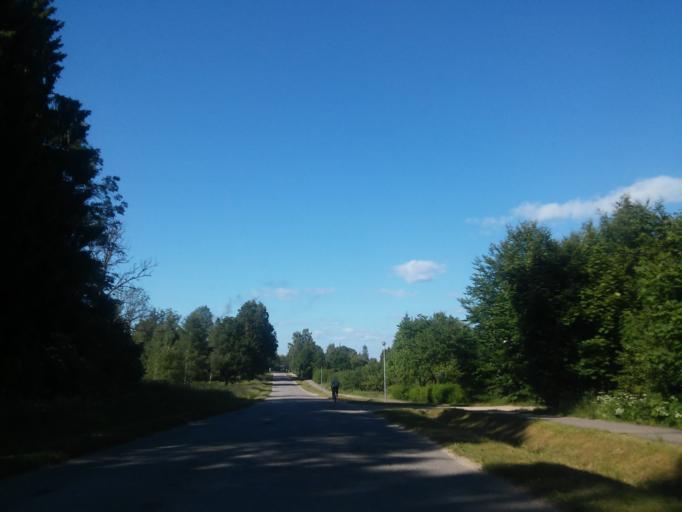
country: LV
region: Vainode
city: Vainode
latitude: 56.4281
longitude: 21.8678
